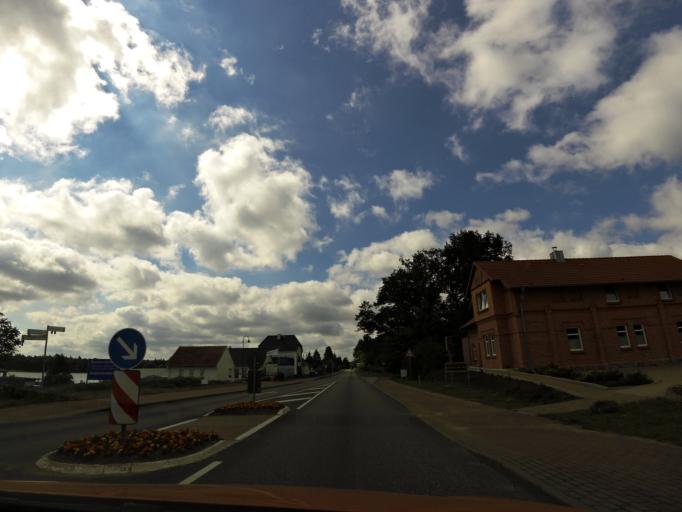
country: DE
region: Mecklenburg-Vorpommern
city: Krakow am See
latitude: 53.6681
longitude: 12.2681
